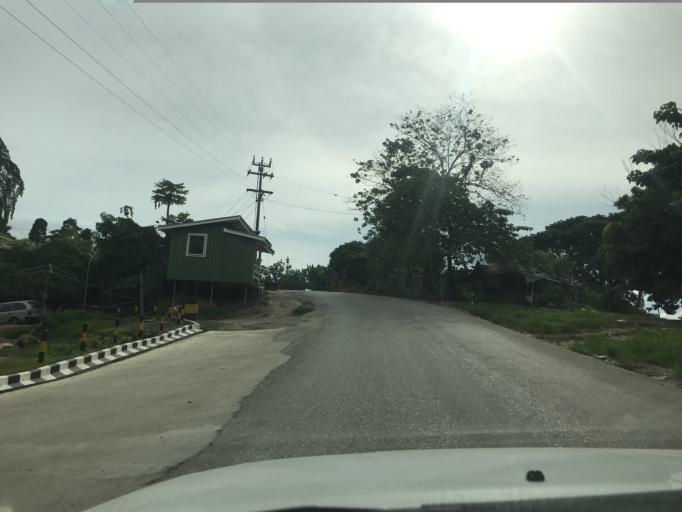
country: SB
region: Guadalcanal
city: Honiara
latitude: -9.4368
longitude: 159.9444
